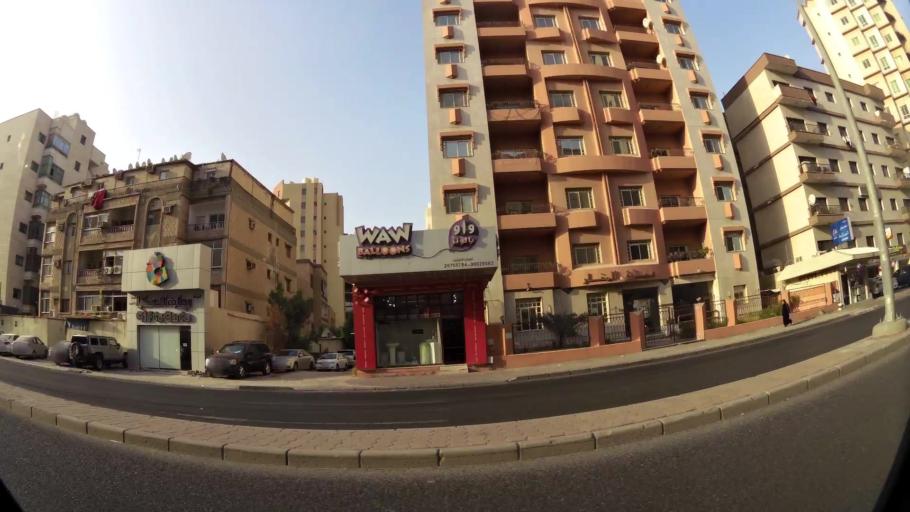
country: KW
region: Muhafazat Hawalli
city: As Salimiyah
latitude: 29.3321
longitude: 48.0617
